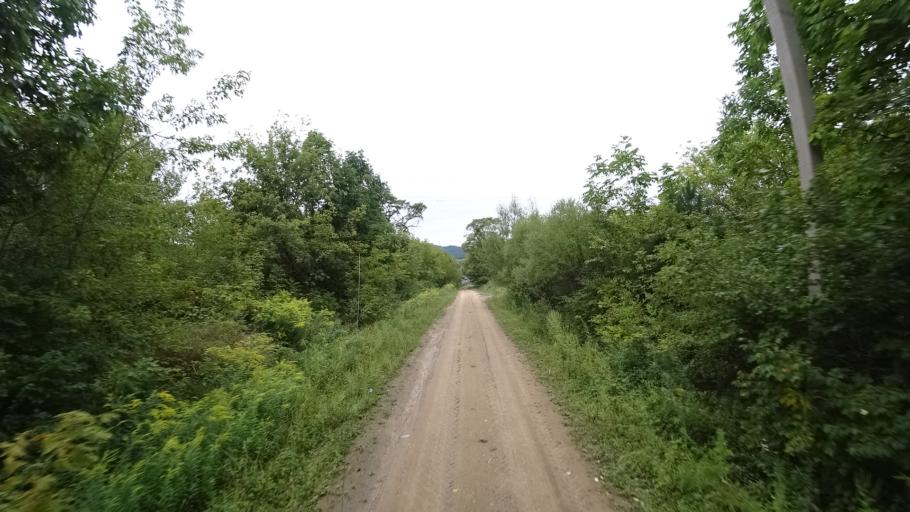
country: RU
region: Primorskiy
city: Rettikhovka
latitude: 44.1593
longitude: 132.7441
